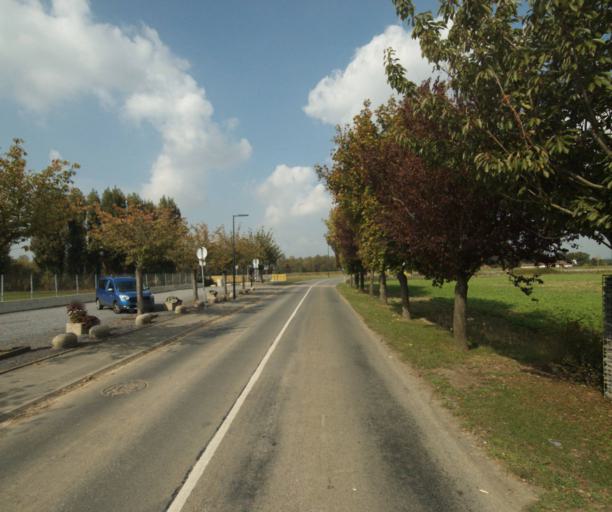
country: FR
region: Nord-Pas-de-Calais
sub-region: Departement du Nord
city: Emmerin
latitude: 50.5800
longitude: 3.0121
